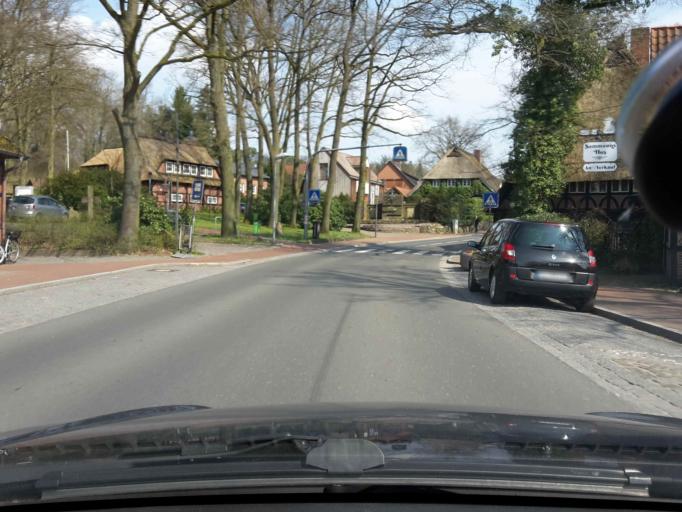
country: DE
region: Lower Saxony
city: Jesteburg
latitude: 53.3077
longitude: 9.9550
